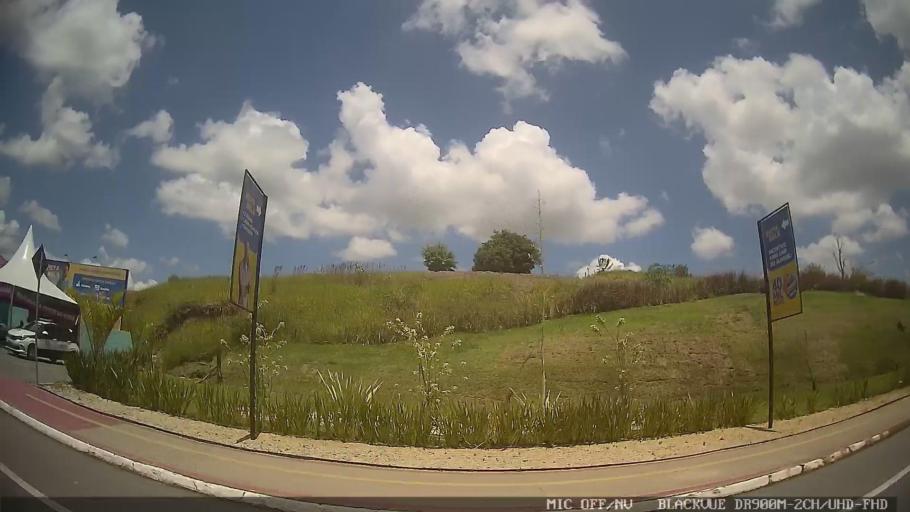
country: BR
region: Sao Paulo
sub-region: Jacarei
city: Jacarei
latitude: -23.3114
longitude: -45.9400
